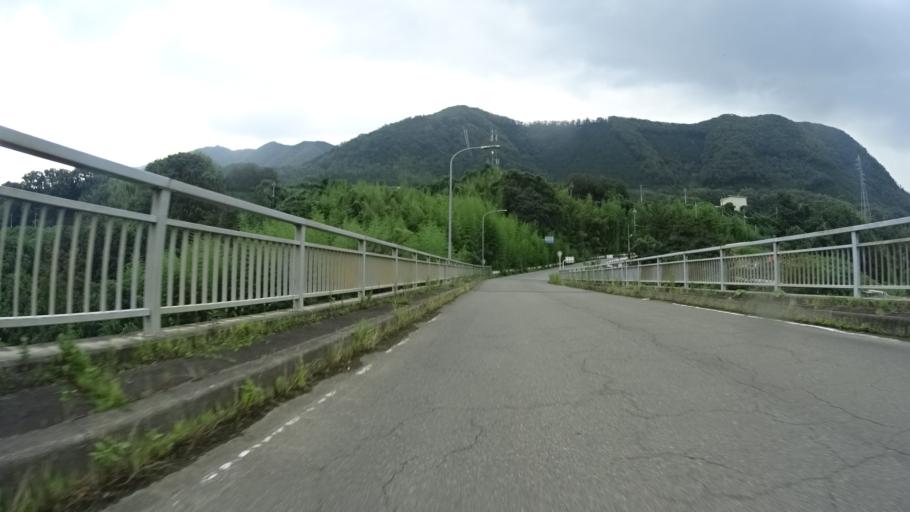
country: JP
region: Yamanashi
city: Enzan
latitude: 35.7445
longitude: 138.7212
